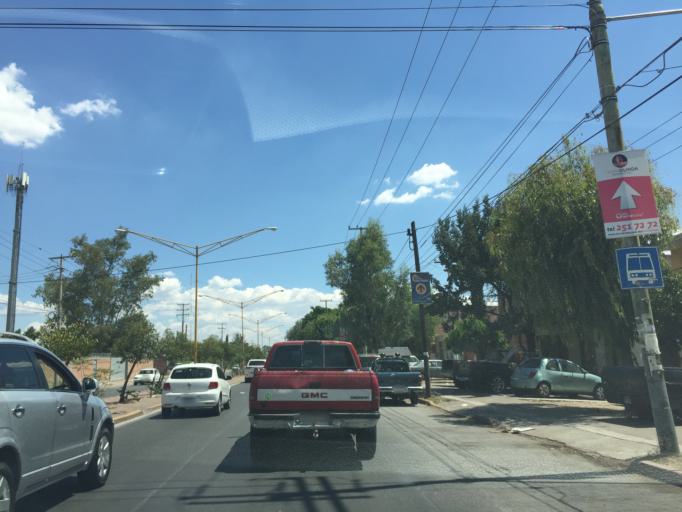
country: MX
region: Aguascalientes
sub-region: Aguascalientes
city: La Loma de los Negritos
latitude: 21.8512
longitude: -102.3184
